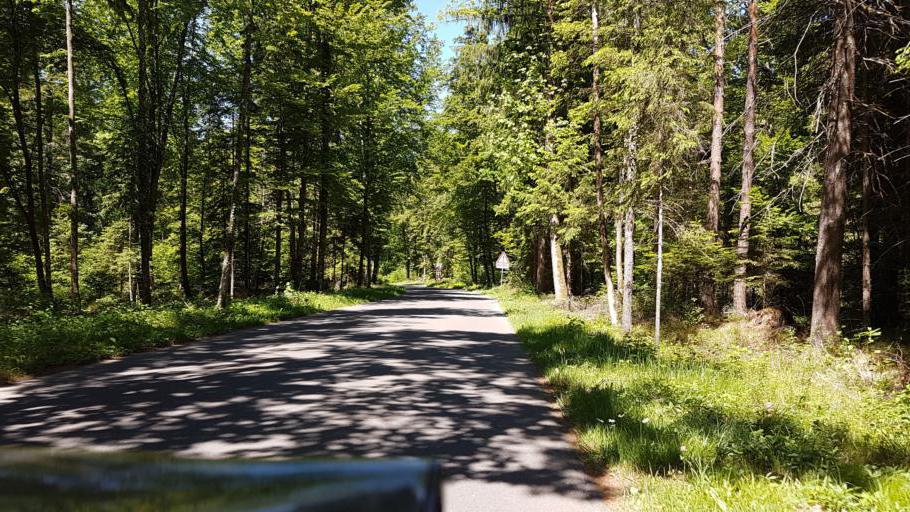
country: CH
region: Bern
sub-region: Thun District
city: Thierachern
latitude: 46.7286
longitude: 7.5954
